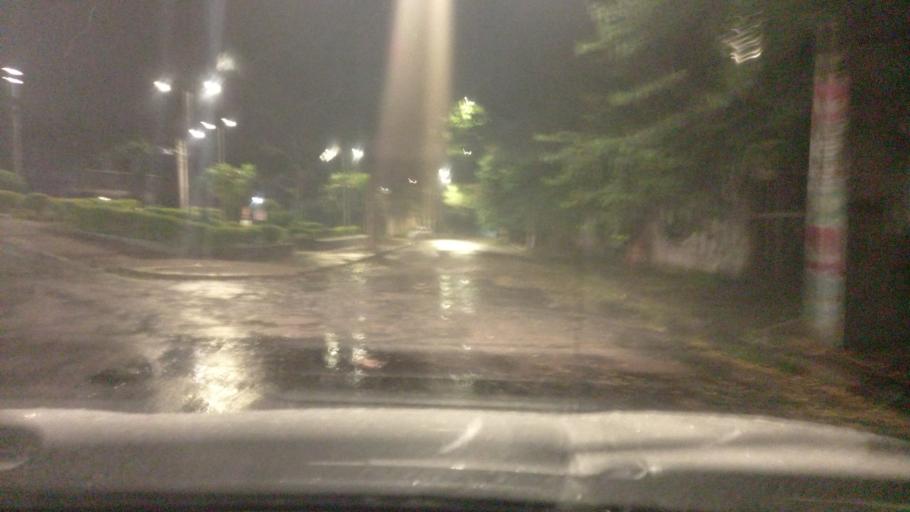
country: BR
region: Minas Gerais
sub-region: Belo Horizonte
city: Belo Horizonte
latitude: -19.9152
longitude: -43.9098
